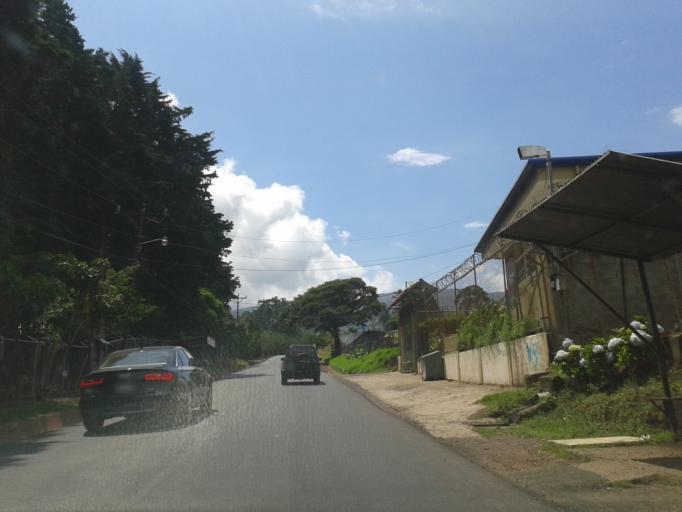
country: CR
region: Alajuela
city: Sabanilla
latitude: 10.1267
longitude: -84.1907
